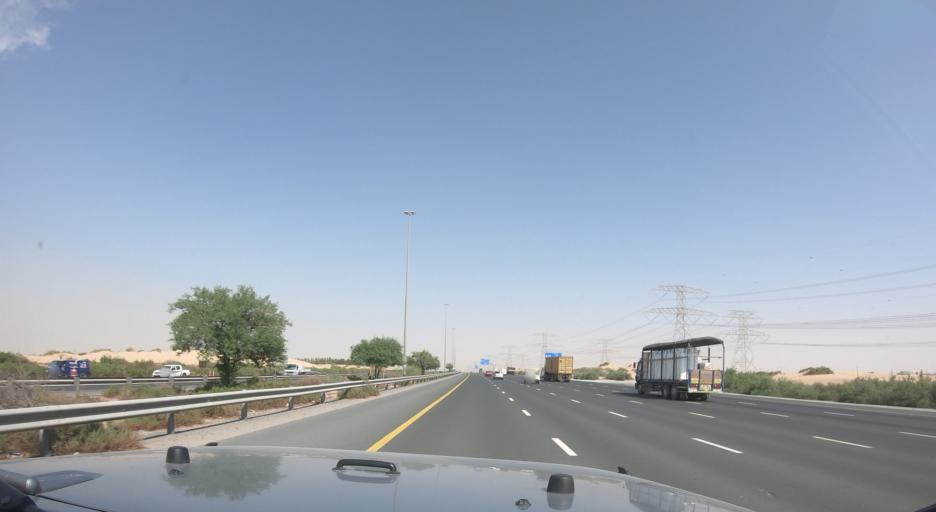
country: AE
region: Ash Shariqah
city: Sharjah
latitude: 25.2012
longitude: 55.5446
